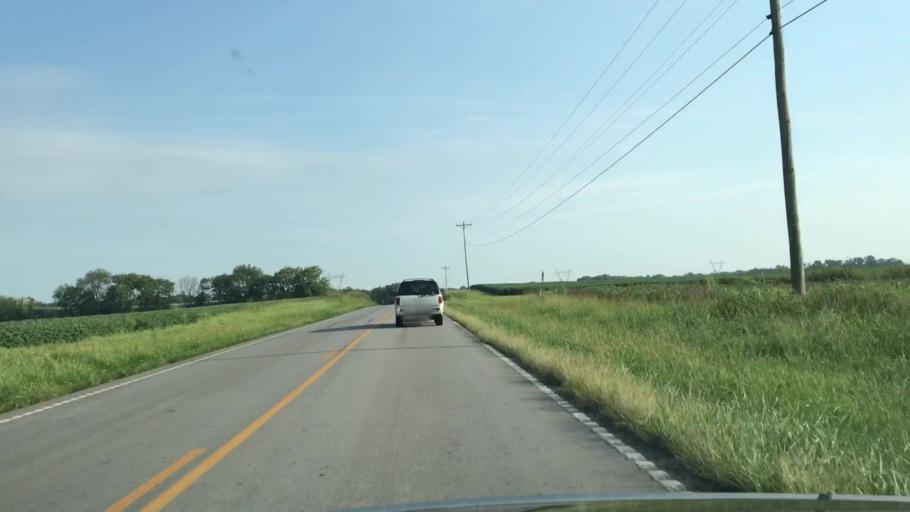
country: US
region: Kentucky
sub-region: Todd County
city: Guthrie
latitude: 36.6611
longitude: -87.1989
